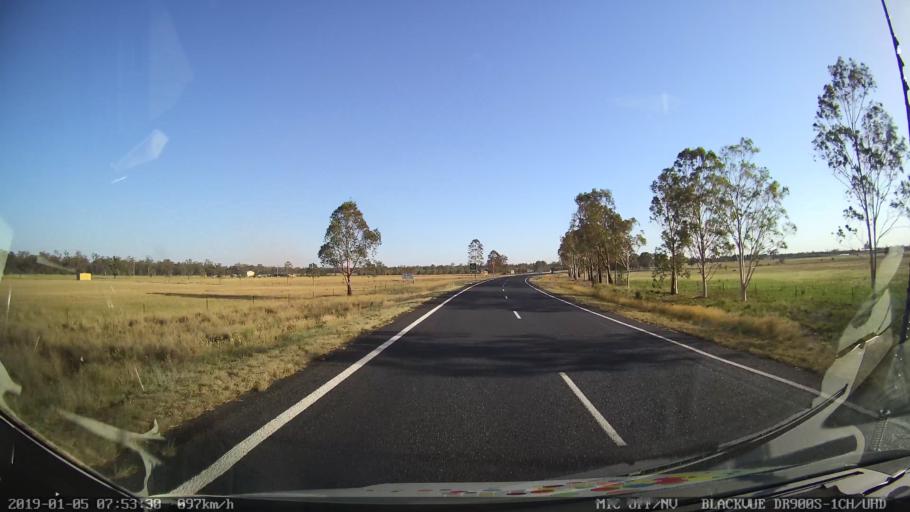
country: AU
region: New South Wales
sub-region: Gilgandra
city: Gilgandra
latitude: -31.7434
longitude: 148.6419
